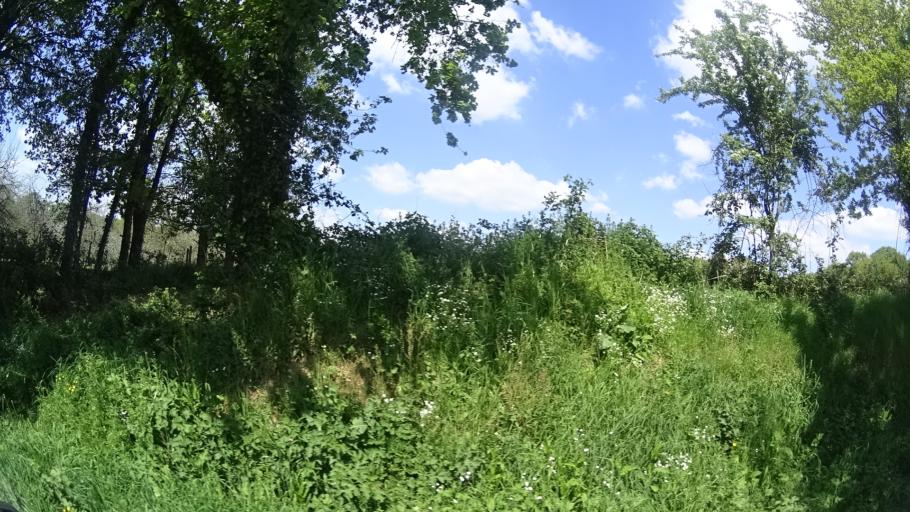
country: FR
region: Brittany
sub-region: Departement du Morbihan
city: Allaire
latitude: 47.6005
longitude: -2.1716
